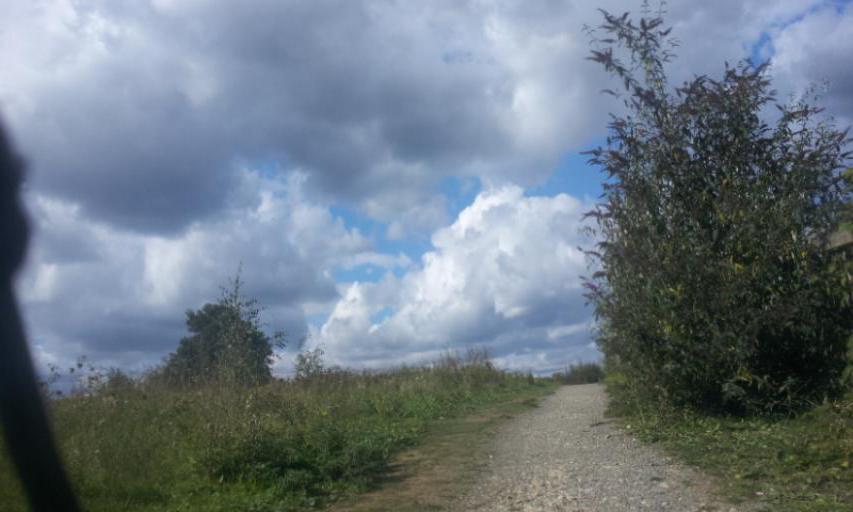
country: GB
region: England
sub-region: Kent
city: West Malling
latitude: 51.3023
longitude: 0.4157
